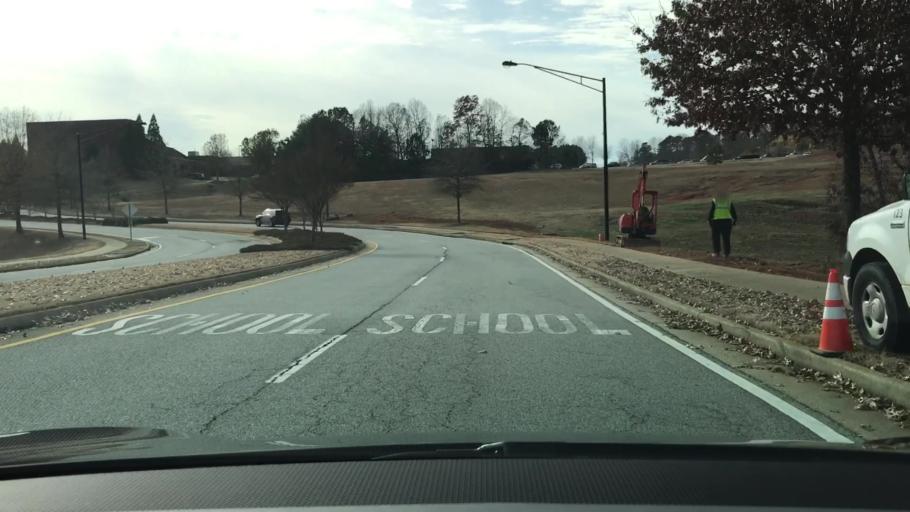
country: US
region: Georgia
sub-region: Gwinnett County
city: Buford
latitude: 34.1313
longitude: -83.9885
